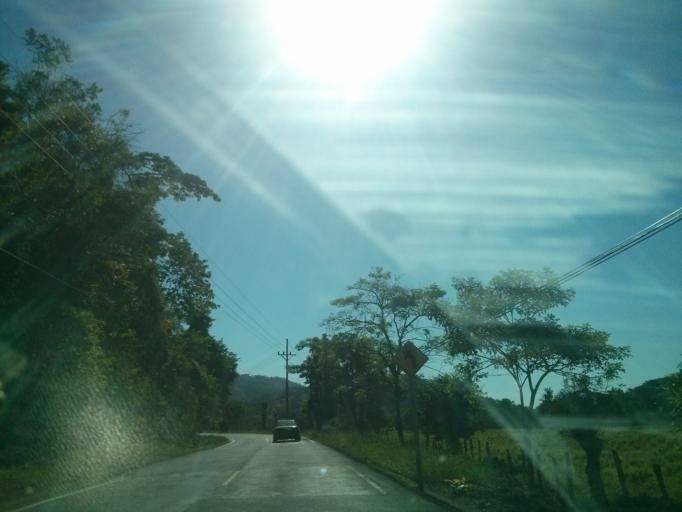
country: CR
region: Puntarenas
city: Paquera
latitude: 9.7546
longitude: -84.9967
